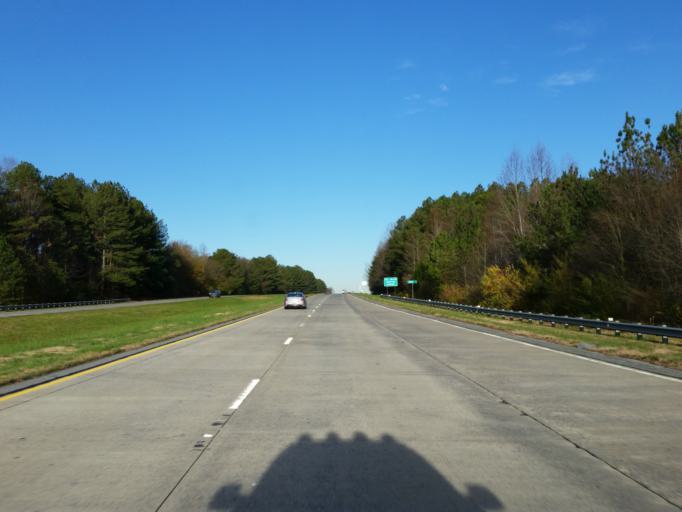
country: US
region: Georgia
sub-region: Pickens County
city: Nelson
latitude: 34.3858
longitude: -84.3985
